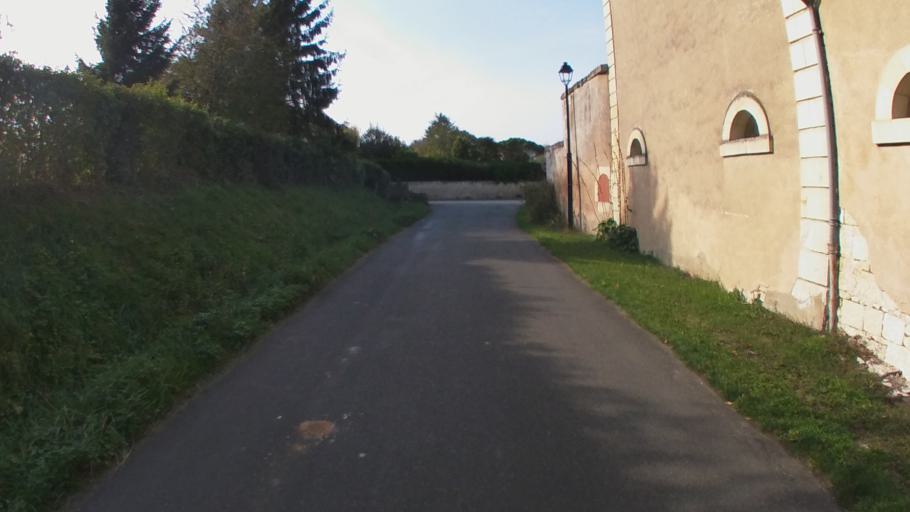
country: FR
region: Pays de la Loire
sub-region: Departement de Maine-et-Loire
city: Distre
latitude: 47.1977
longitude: -0.1164
